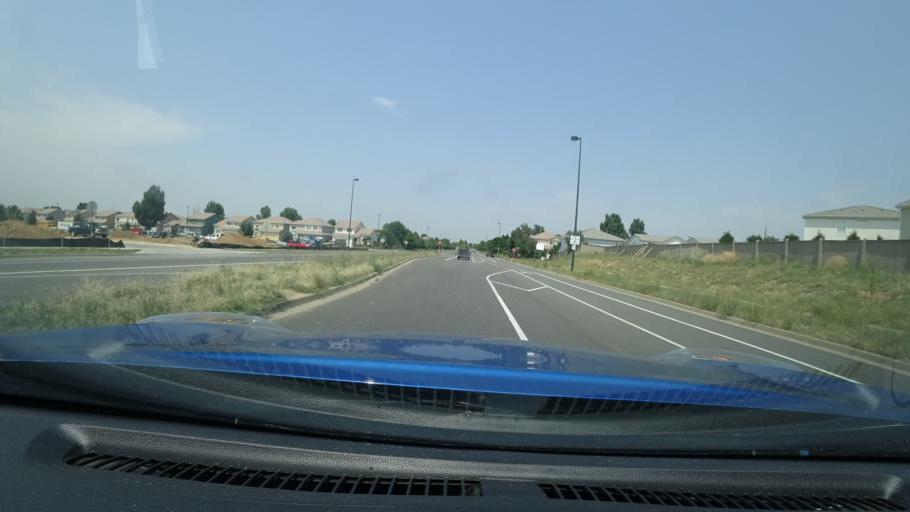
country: US
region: Colorado
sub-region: Adams County
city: Aurora
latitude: 39.7699
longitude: -104.7534
